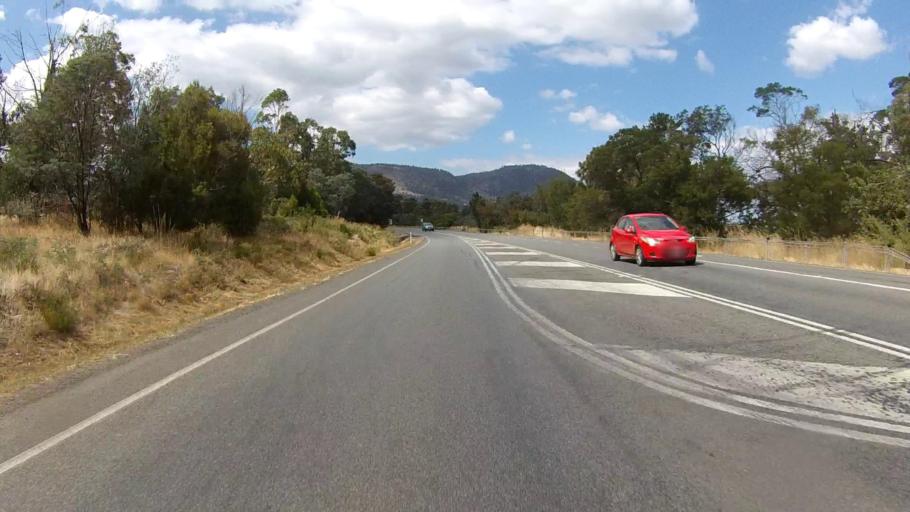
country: AU
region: Tasmania
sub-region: Brighton
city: Old Beach
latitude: -42.7773
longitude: 147.2718
